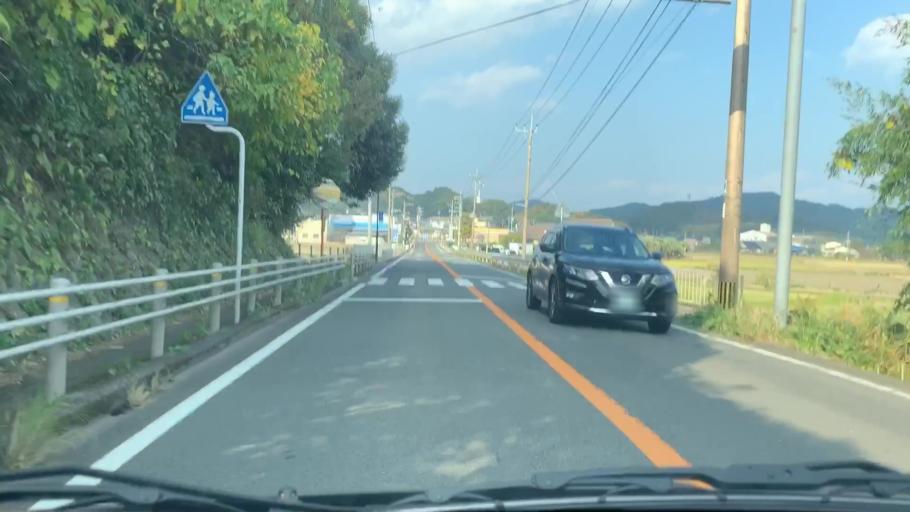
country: JP
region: Nagasaki
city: Togitsu
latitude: 32.9425
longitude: 129.7821
